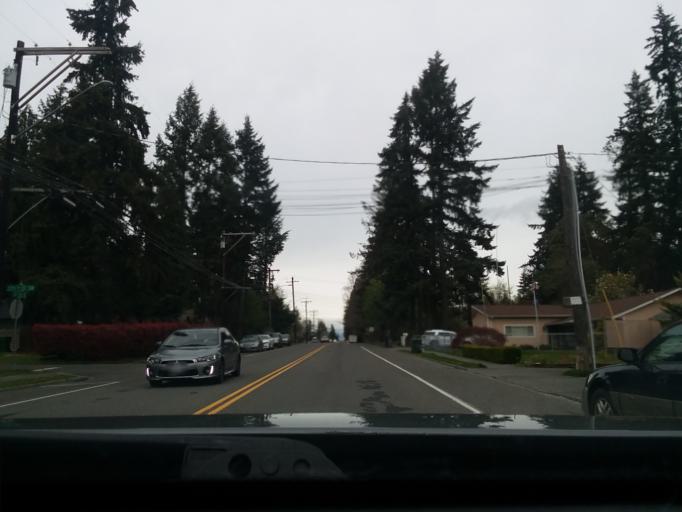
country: US
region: Washington
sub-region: Snohomish County
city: Mountlake Terrace
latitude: 47.7946
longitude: -122.3085
